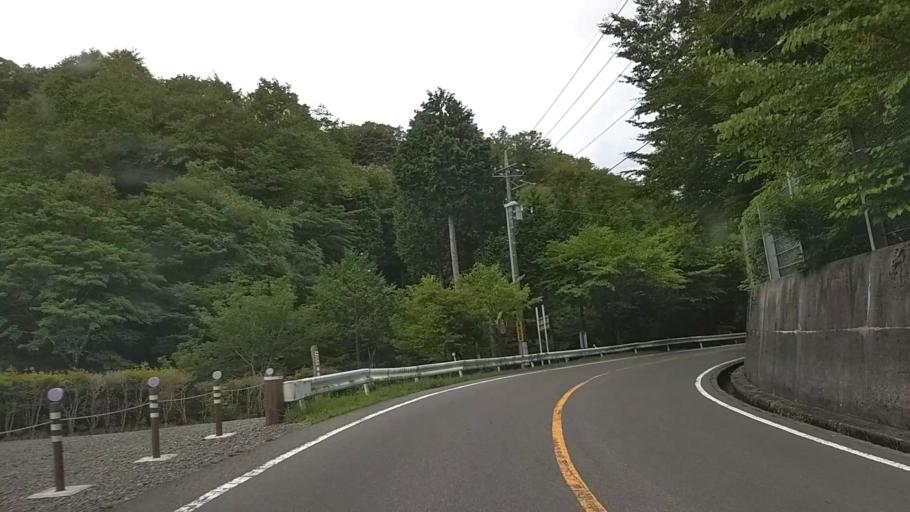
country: JP
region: Yamanashi
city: Otsuki
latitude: 35.4555
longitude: 138.9369
